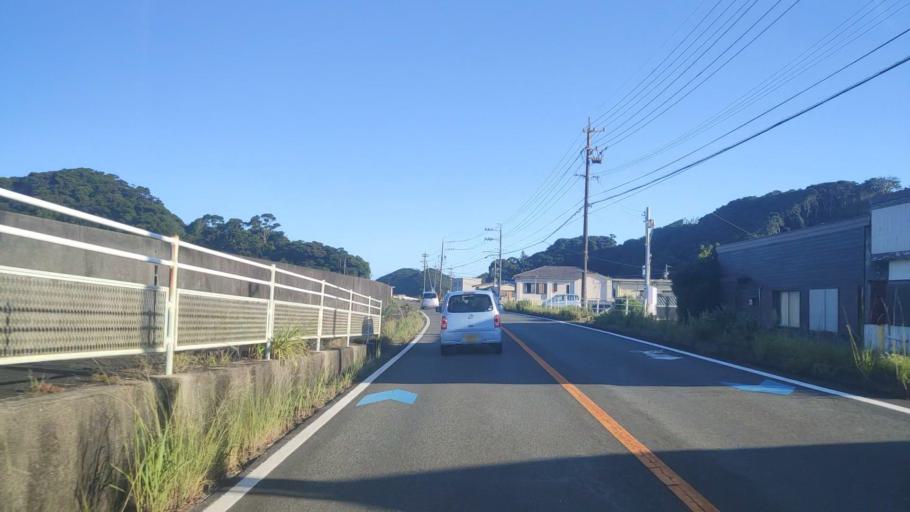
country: JP
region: Mie
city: Toba
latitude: 34.2702
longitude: 136.8683
